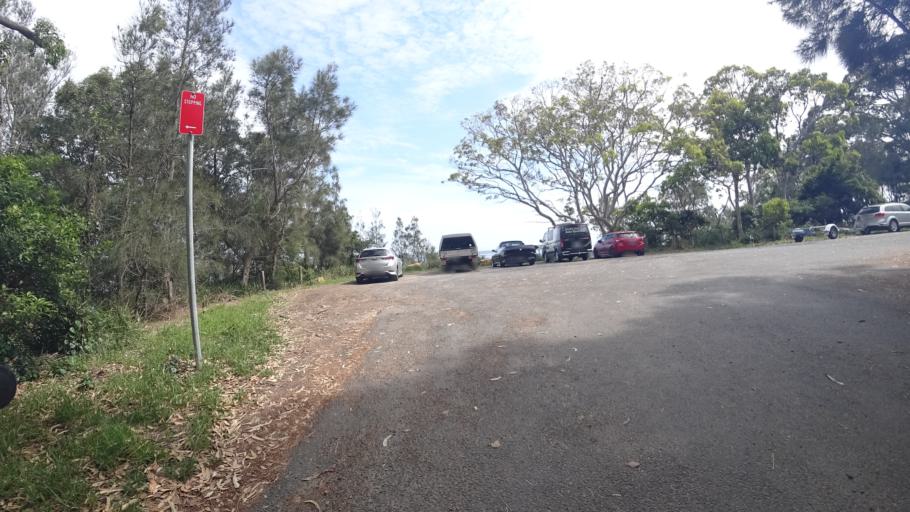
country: AU
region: New South Wales
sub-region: Shoalhaven Shire
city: Milton
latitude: -35.2443
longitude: 150.5396
